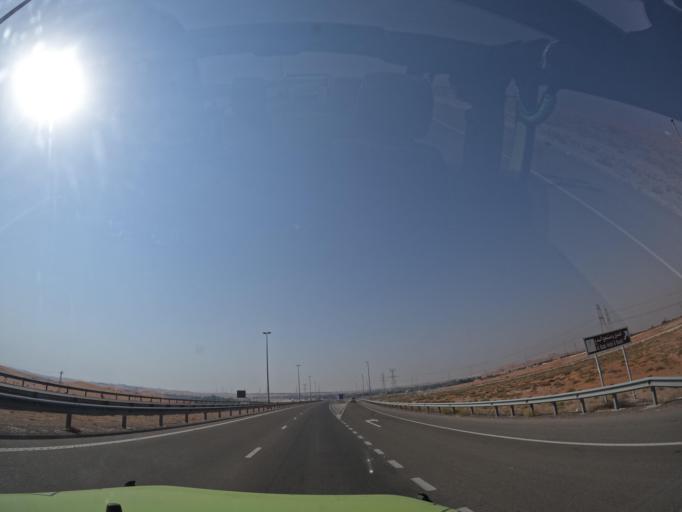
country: OM
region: Al Buraimi
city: Al Buraymi
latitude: 24.3734
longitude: 55.7284
